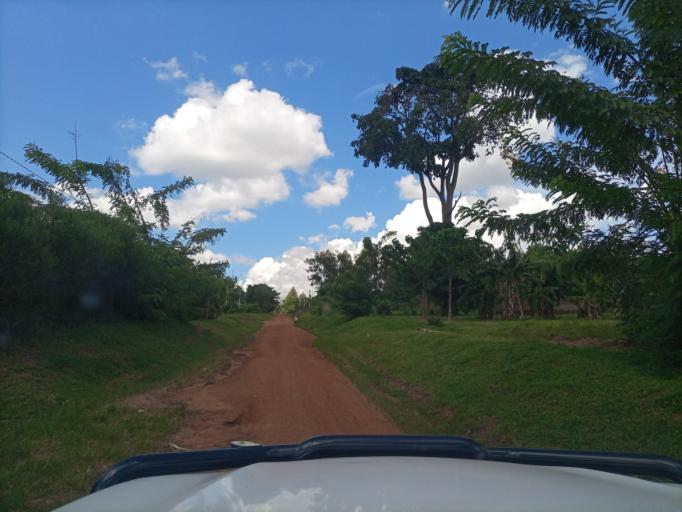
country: UG
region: Eastern Region
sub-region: Tororo District
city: Tororo
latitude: 0.7055
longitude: 34.0137
